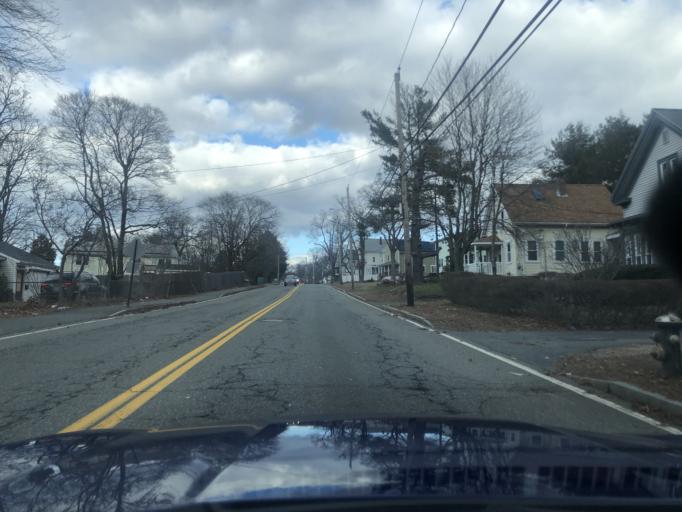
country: US
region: Massachusetts
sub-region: Plymouth County
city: Brockton
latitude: 42.0983
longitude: -71.0086
